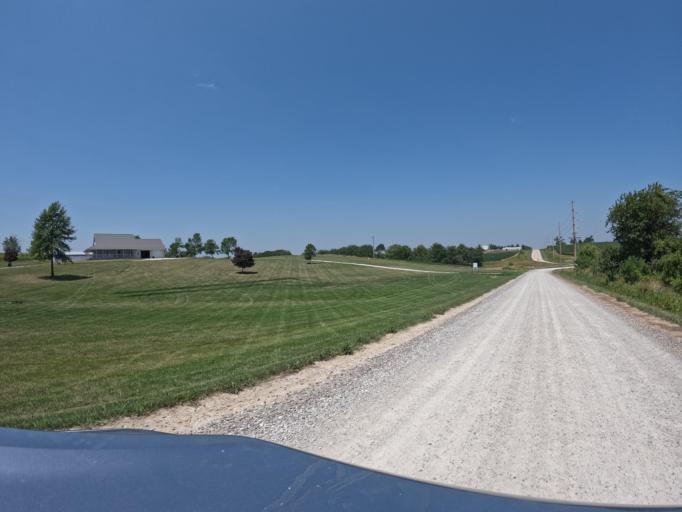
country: US
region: Iowa
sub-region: Keokuk County
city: Sigourney
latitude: 41.2751
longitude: -92.1806
